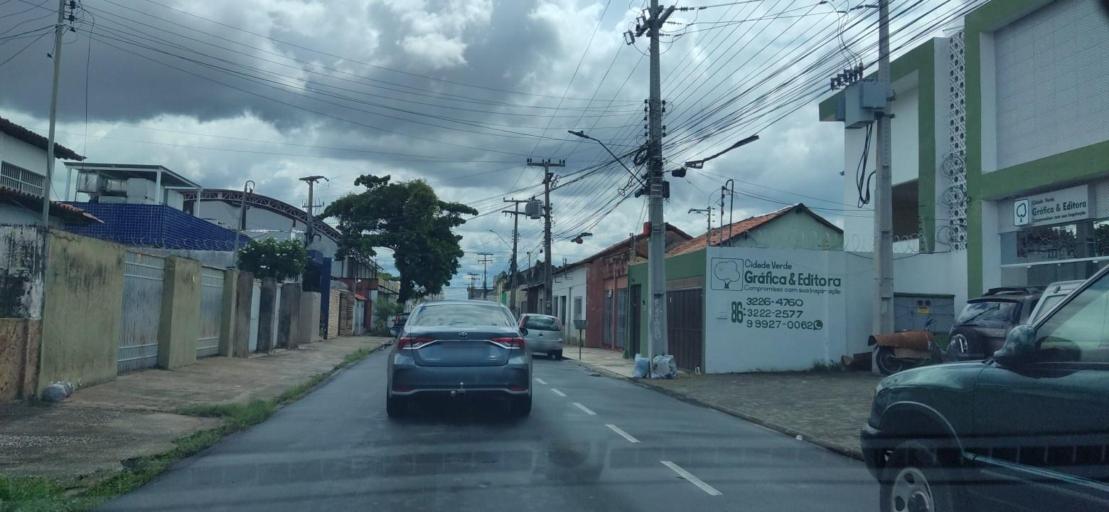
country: BR
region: Piaui
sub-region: Teresina
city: Teresina
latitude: -5.0849
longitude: -42.8098
